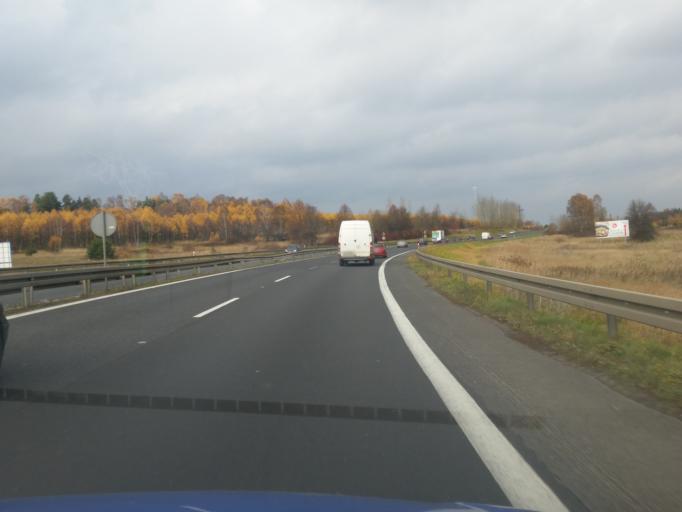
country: PL
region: Silesian Voivodeship
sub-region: Powiat czestochowski
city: Kamienica Polska
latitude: 50.6329
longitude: 19.1369
